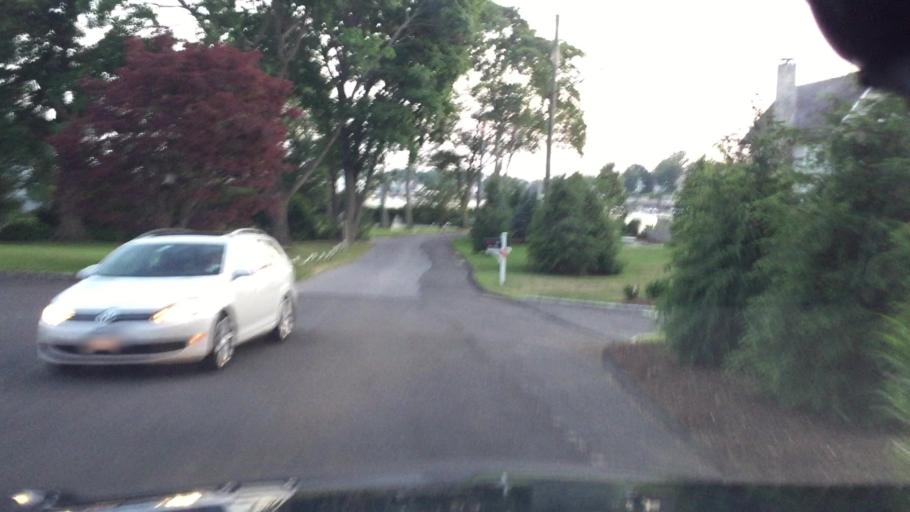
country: US
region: Connecticut
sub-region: Fairfield County
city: Darien
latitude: 41.0648
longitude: -73.4280
